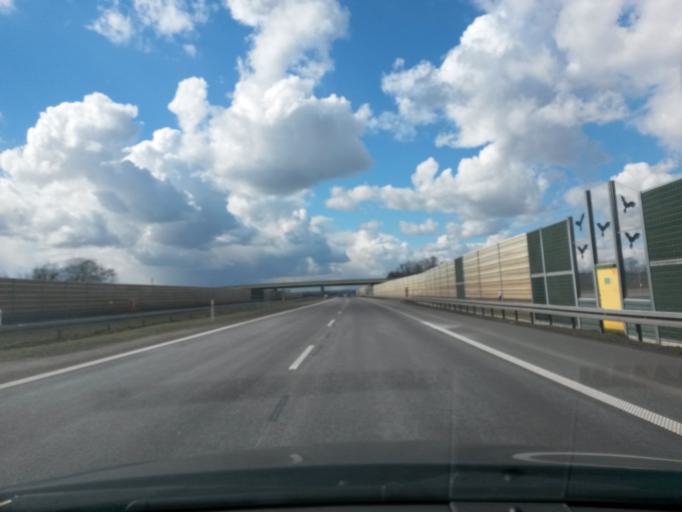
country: PL
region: Greater Poland Voivodeship
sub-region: Powiat turecki
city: Brudzew
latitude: 52.1293
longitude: 18.6615
